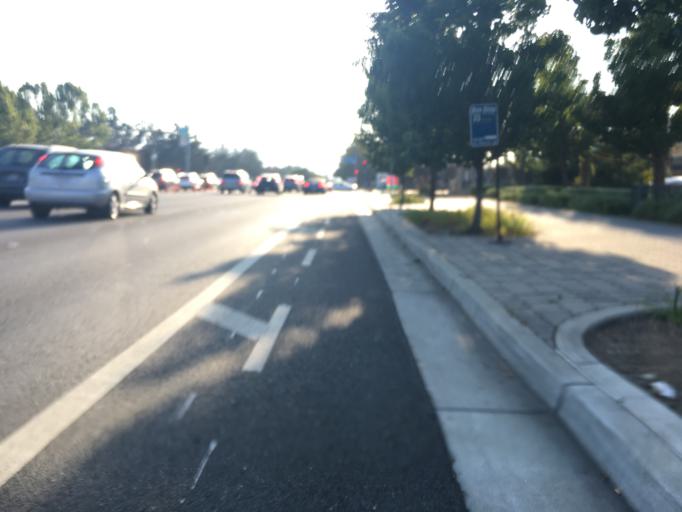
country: US
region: California
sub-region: Santa Clara County
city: Cupertino
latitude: 37.3229
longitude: -122.0403
